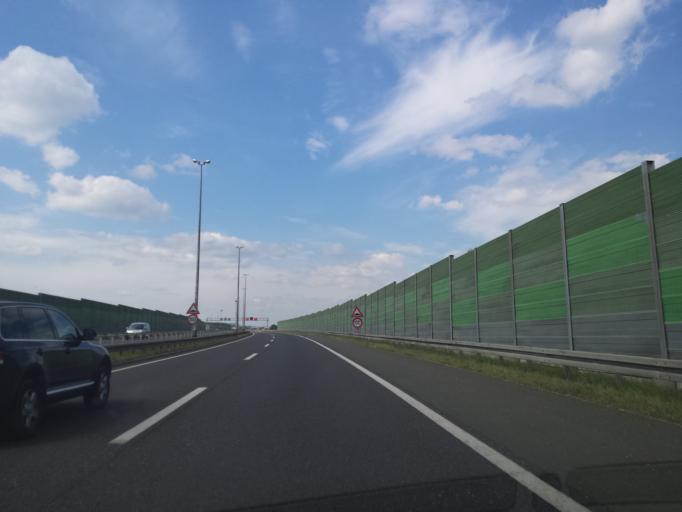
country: HR
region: Grad Zagreb
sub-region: Sesvete
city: Sesvete
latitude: 45.8148
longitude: 16.1373
